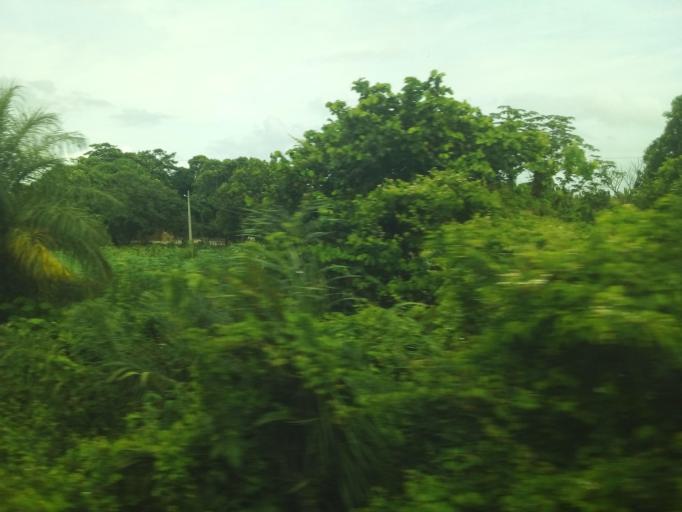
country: BR
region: Maranhao
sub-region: Itapecuru Mirim
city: Itapecuru Mirim
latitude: -3.3222
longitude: -44.4836
